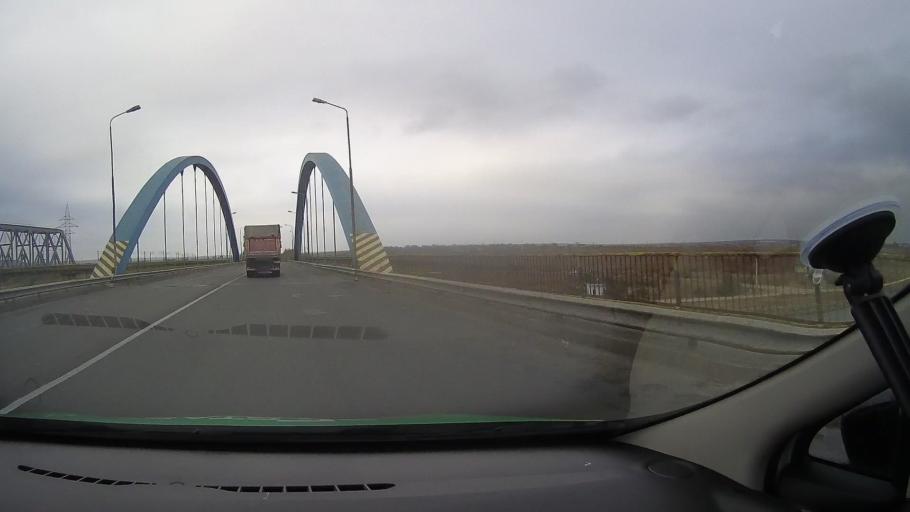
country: RO
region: Constanta
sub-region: Comuna Poarta Alba
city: Poarta Alba
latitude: 44.2168
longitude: 28.3894
